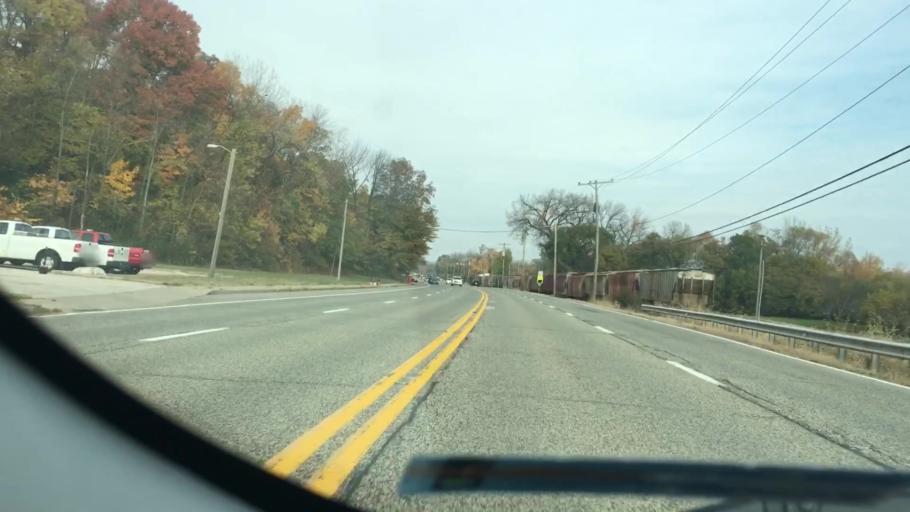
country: US
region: Illinois
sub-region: Peoria County
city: Peoria Heights
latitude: 40.7423
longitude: -89.5546
